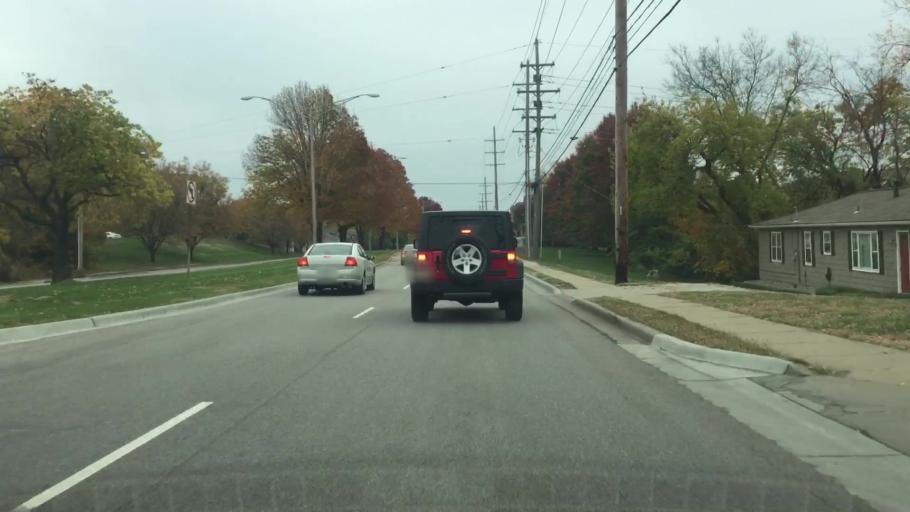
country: US
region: Kansas
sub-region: Johnson County
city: Lenexa
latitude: 38.9273
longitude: -94.7521
